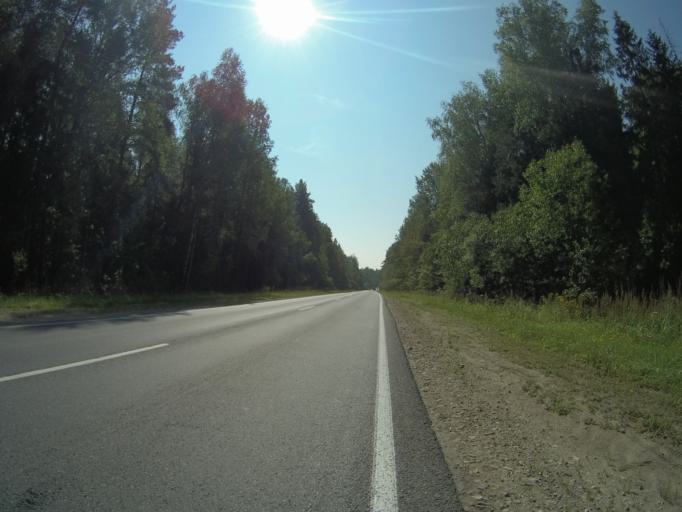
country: RU
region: Vladimir
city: Anopino
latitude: 55.8780
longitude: 40.6248
